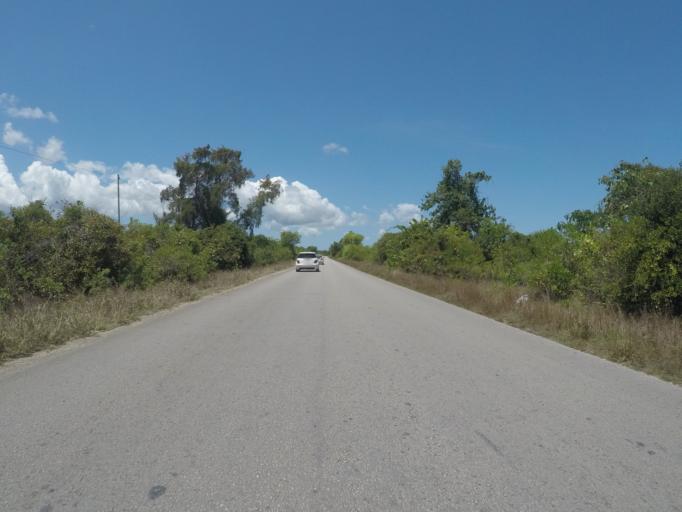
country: TZ
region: Zanzibar Central/South
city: Koani
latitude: -6.2712
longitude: 39.3564
